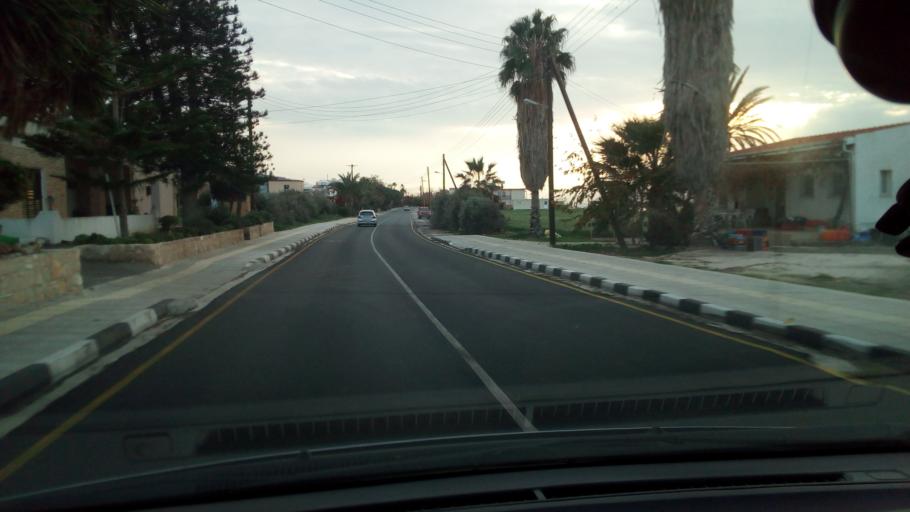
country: CY
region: Pafos
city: Polis
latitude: 35.1139
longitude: 32.5094
